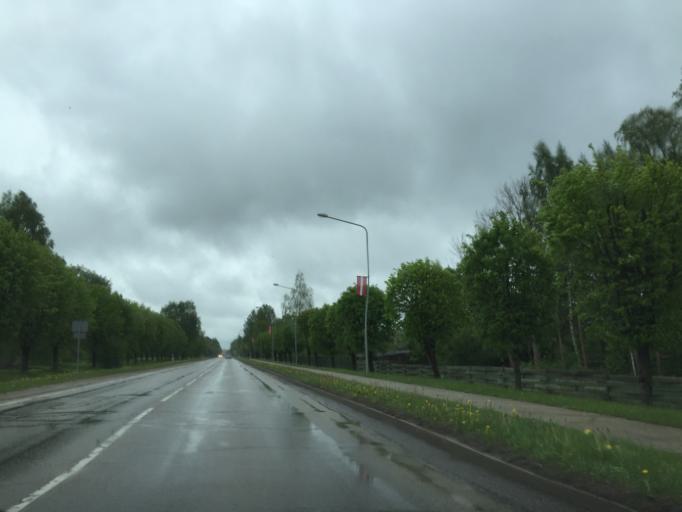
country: LV
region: Lielvarde
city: Lielvarde
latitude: 56.7207
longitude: 24.7854
